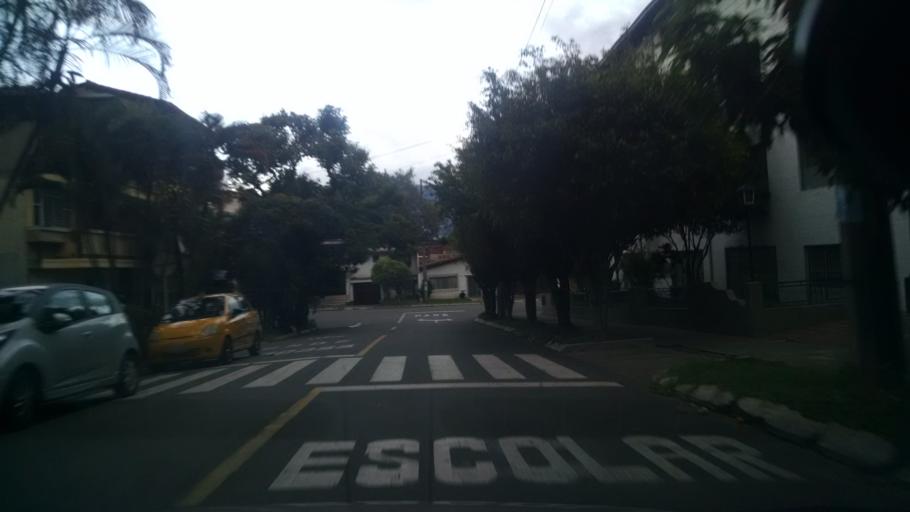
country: CO
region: Antioquia
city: Medellin
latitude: 6.2656
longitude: -75.5988
